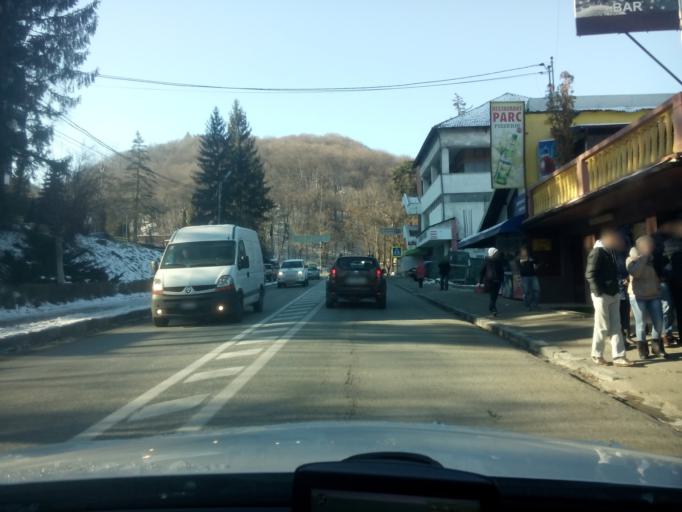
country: RO
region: Valcea
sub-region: Oras Calimanesti
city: Calimanesti
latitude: 45.2597
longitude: 24.3219
